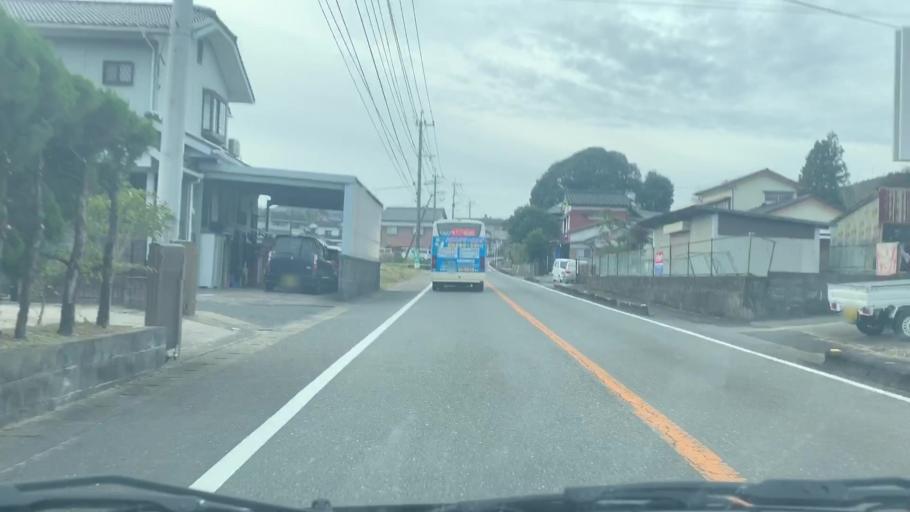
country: JP
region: Saga Prefecture
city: Ureshinomachi-shimojuku
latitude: 33.1225
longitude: 130.0024
